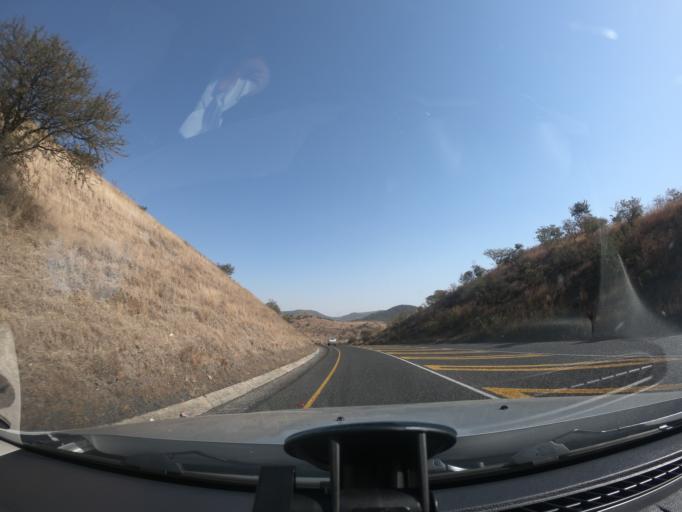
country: ZA
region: KwaZulu-Natal
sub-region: uThukela District Municipality
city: Ladysmith
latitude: -28.6714
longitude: 29.8330
